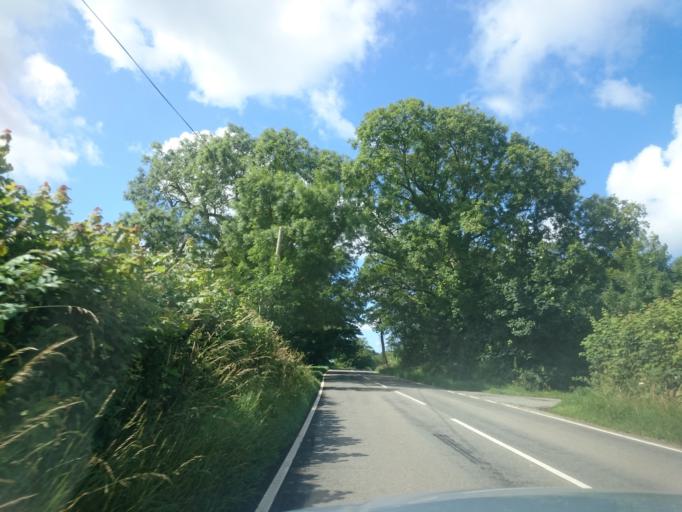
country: GB
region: Wales
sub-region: Pembrokeshire
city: Johnston
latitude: 51.7798
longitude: -4.9999
